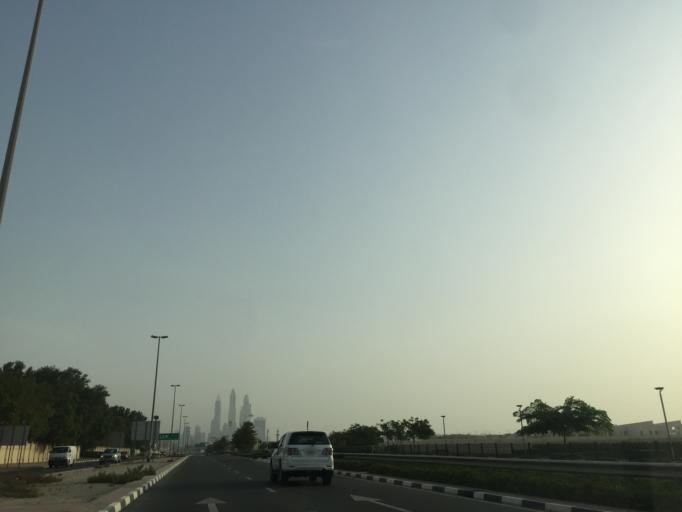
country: AE
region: Dubai
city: Dubai
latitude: 25.1181
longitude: 55.1797
